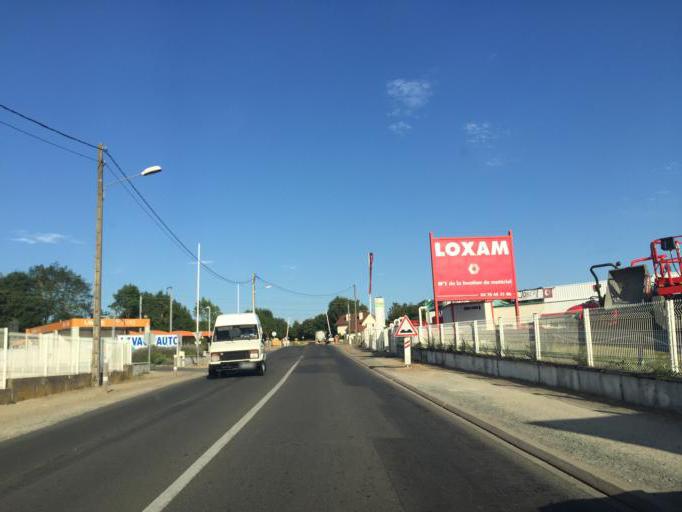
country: FR
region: Auvergne
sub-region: Departement de l'Allier
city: Toulon-sur-Allier
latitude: 46.5363
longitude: 3.3484
